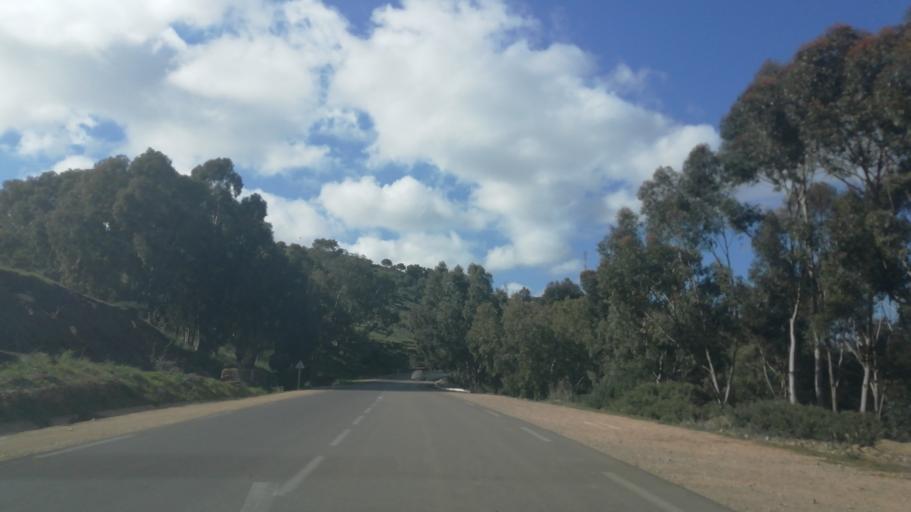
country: DZ
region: Relizane
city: Relizane
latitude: 36.0848
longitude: 0.4759
